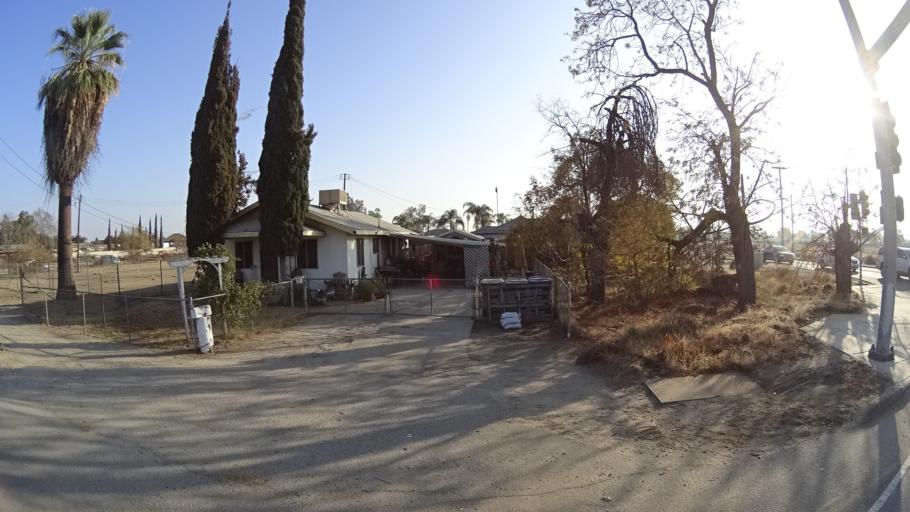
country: US
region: California
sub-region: Kern County
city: Rosedale
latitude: 35.3835
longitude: -119.1542
